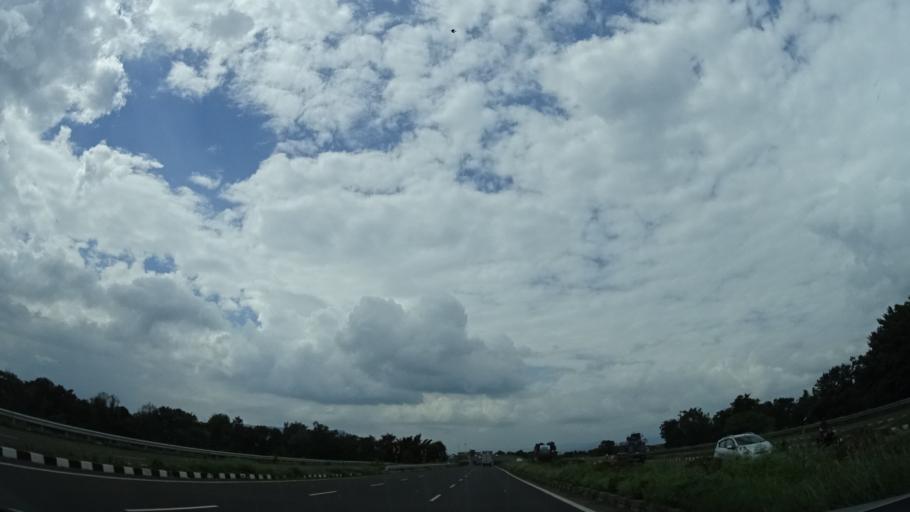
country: IN
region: Maharashtra
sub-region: Satara Division
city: Satara
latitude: 17.8025
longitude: 73.9753
